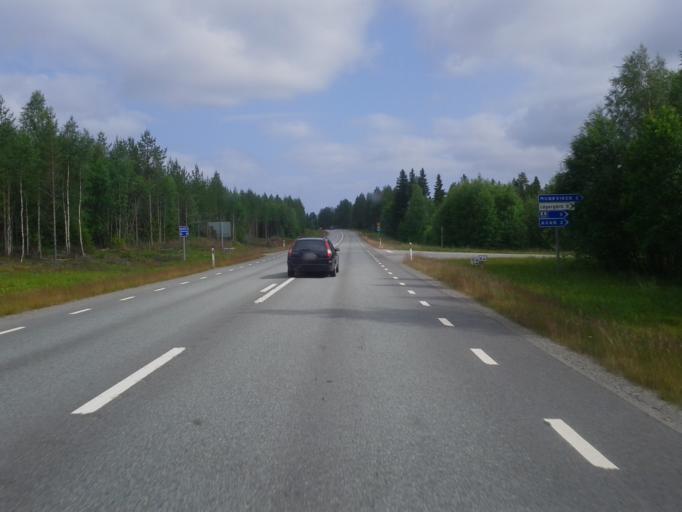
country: SE
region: Vaesterbotten
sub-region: Skelleftea Kommun
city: Burea
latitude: 64.3459
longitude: 21.2874
